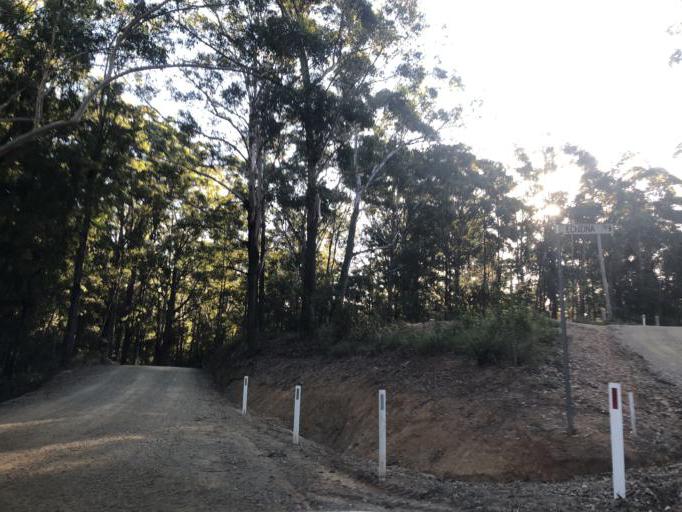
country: AU
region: New South Wales
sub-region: Nambucca Shire
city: Nambucca
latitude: -30.5850
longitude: 152.9301
